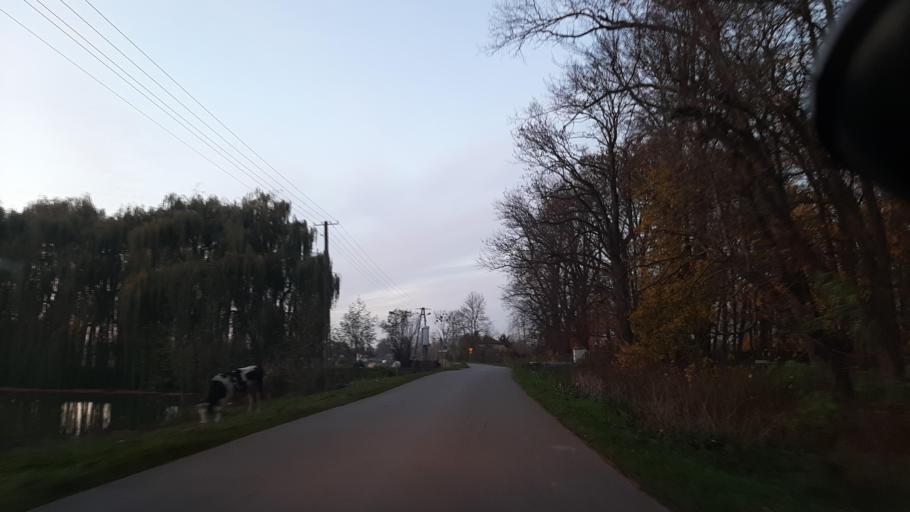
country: PL
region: Lublin Voivodeship
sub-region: Powiat lubelski
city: Jastkow
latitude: 51.3414
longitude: 22.4134
